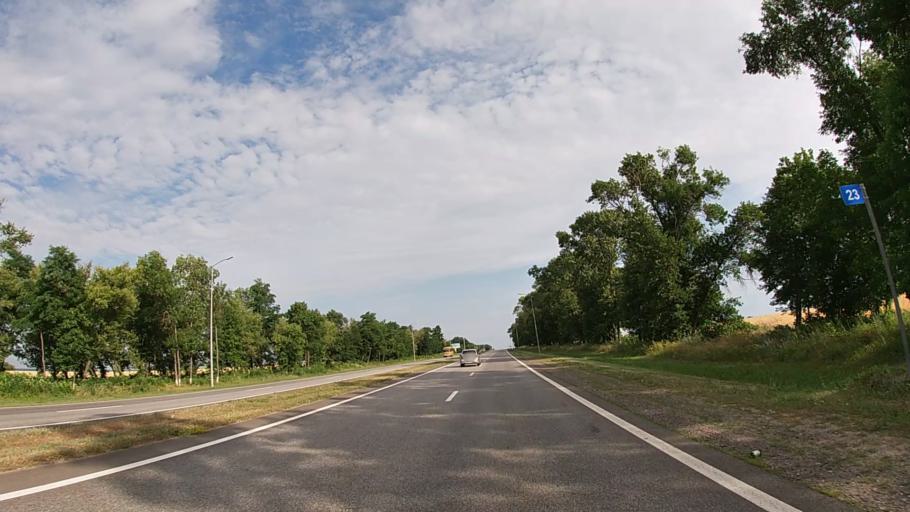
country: RU
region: Belgorod
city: Tomarovka
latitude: 50.6763
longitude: 36.2928
